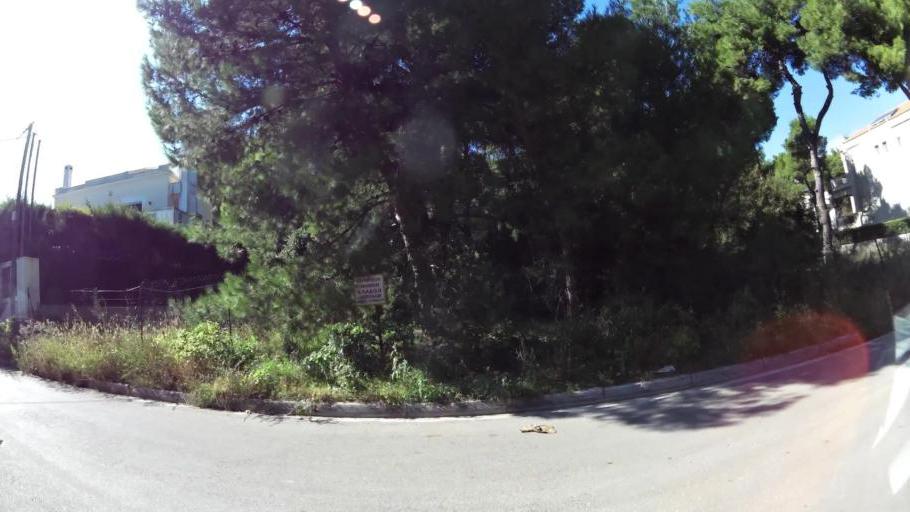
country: GR
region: Attica
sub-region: Nomarchia Anatolikis Attikis
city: Drosia
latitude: 38.1173
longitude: 23.8571
